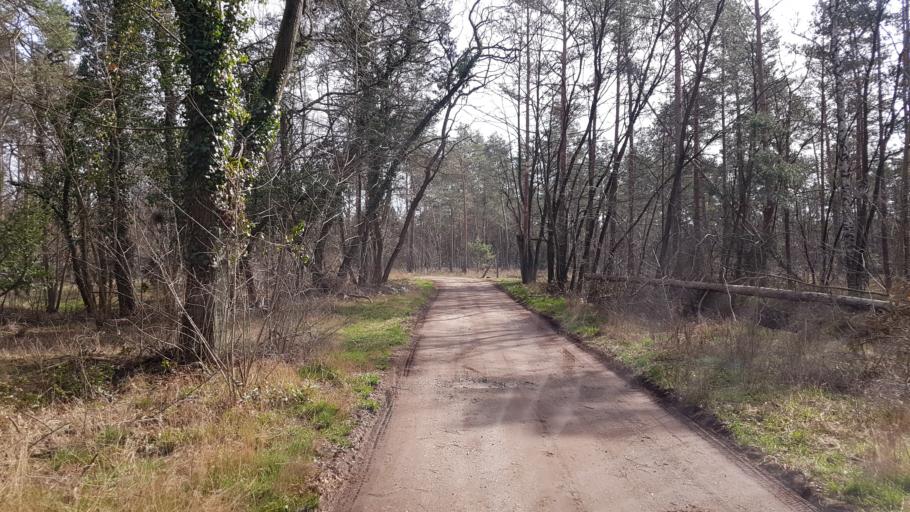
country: DE
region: Brandenburg
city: Doberlug-Kirchhain
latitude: 51.6253
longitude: 13.6127
